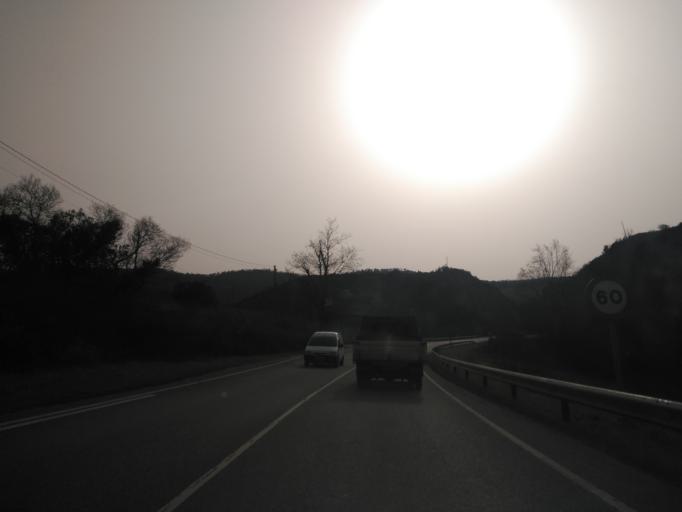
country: ES
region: Cantabria
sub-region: Provincia de Cantabria
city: Comillas
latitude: 43.3630
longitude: -4.2692
